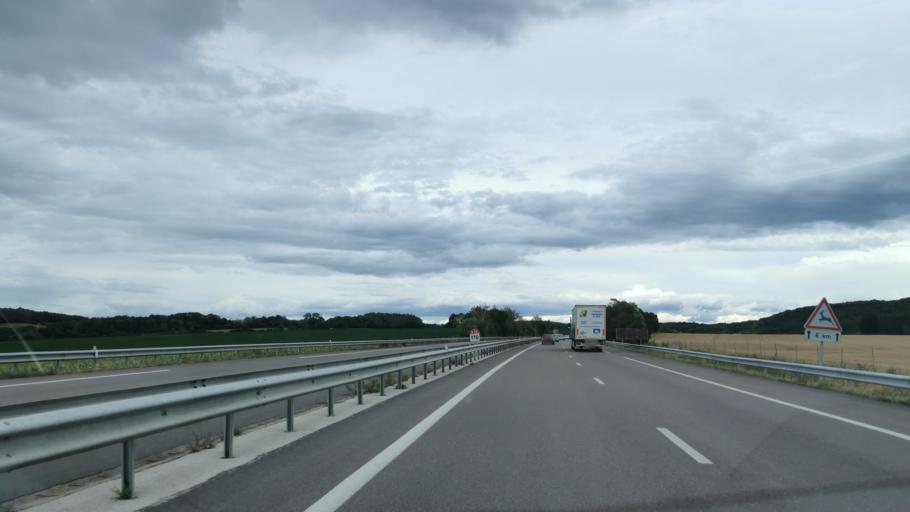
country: FR
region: Franche-Comte
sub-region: Departement du Jura
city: Champvans
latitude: 47.1345
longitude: 5.4601
